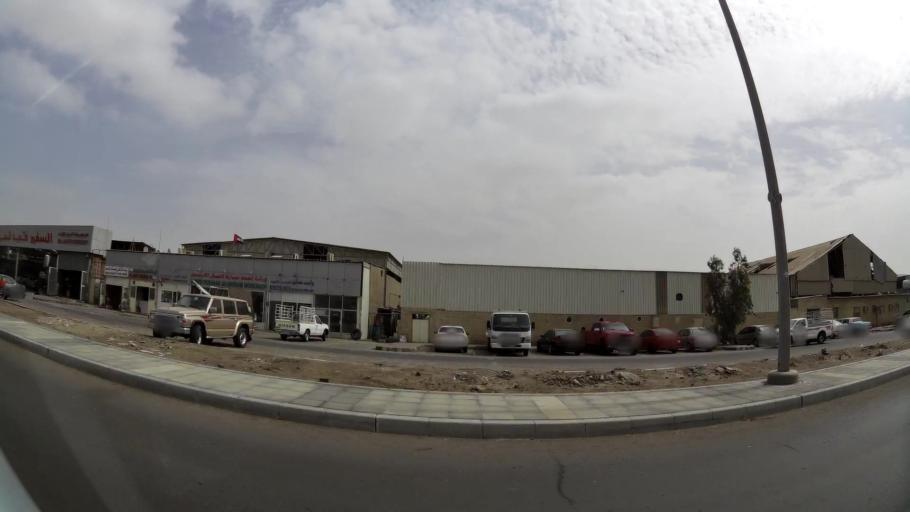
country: AE
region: Abu Dhabi
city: Abu Dhabi
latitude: 24.3792
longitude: 54.5110
